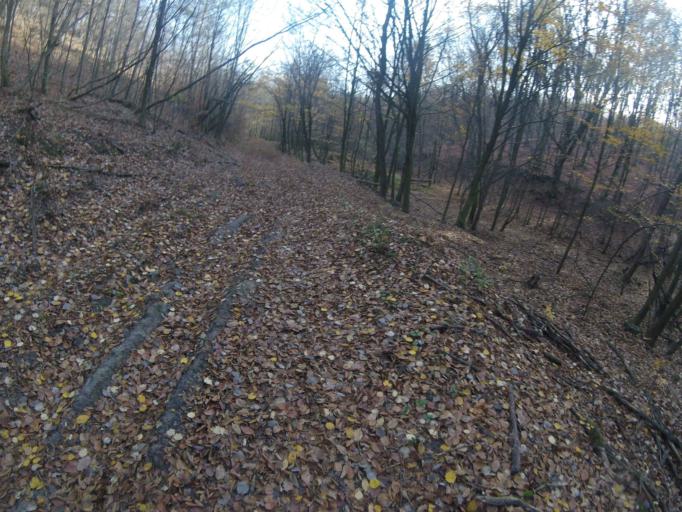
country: HU
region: Borsod-Abauj-Zemplen
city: Sarospatak
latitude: 48.4306
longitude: 21.5104
